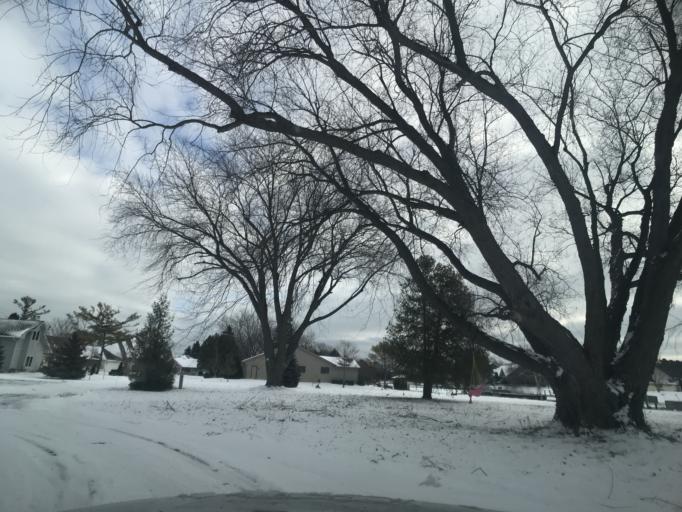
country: US
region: Wisconsin
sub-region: Door County
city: Sturgeon Bay
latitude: 44.8226
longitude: -87.3699
